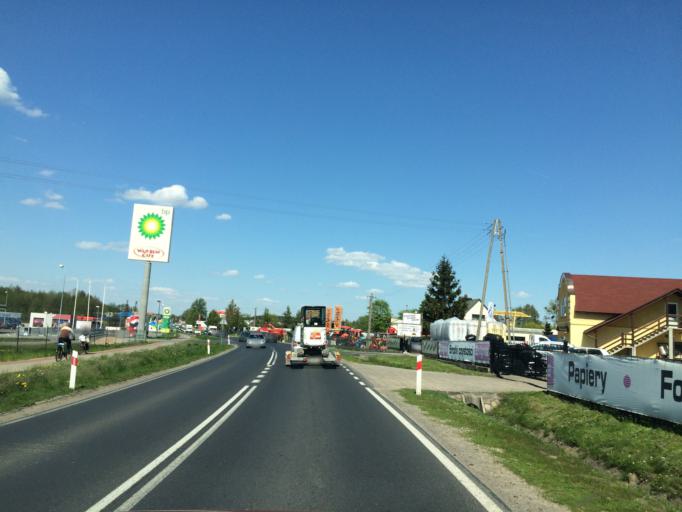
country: PL
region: Warmian-Masurian Voivodeship
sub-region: Powiat nowomiejski
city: Nowe Miasto Lubawskie
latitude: 53.4062
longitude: 19.5928
